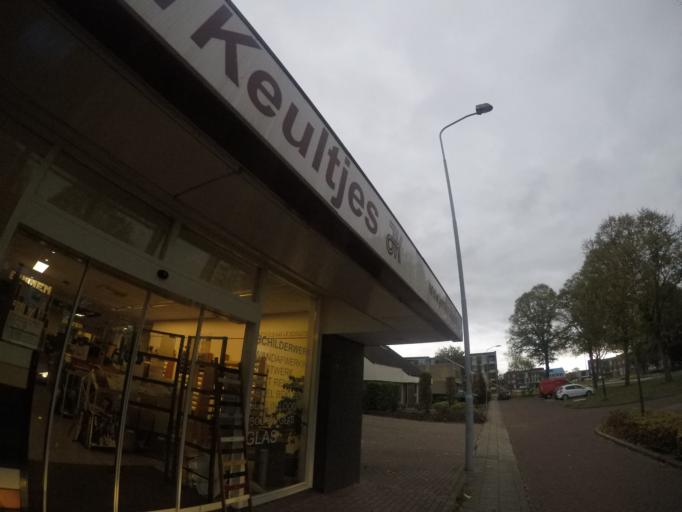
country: NL
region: Gelderland
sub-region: Gemeente Zevenaar
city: Zevenaar
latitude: 51.9328
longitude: 6.0759
